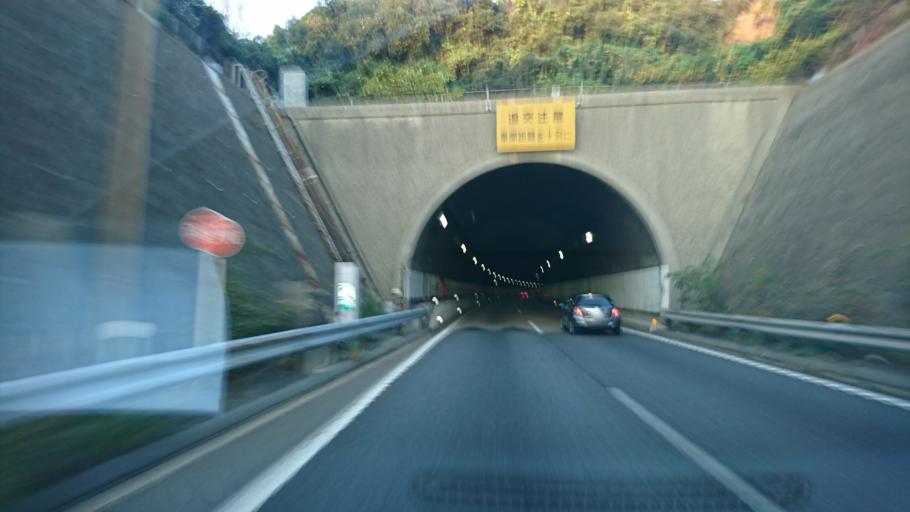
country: JP
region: Hyogo
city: Kobe
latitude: 34.6499
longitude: 135.1030
